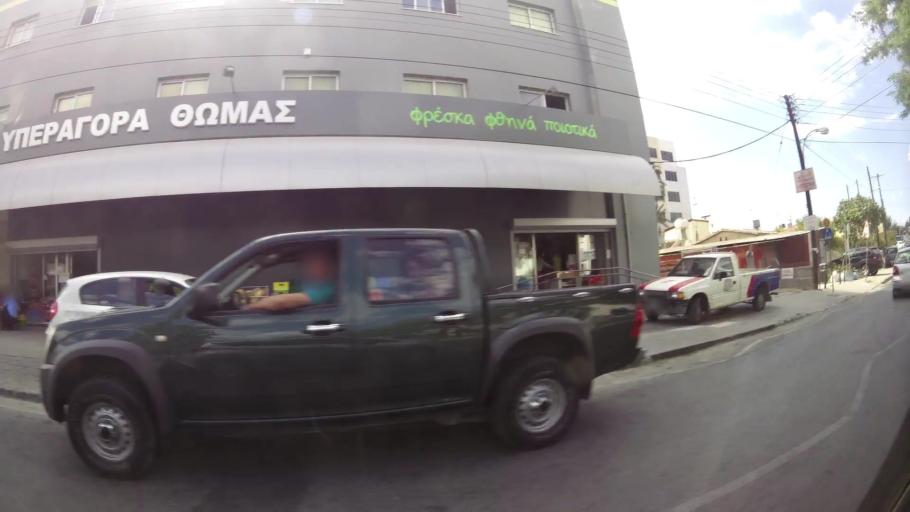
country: CY
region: Lefkosia
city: Nicosia
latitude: 35.1813
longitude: 33.3867
